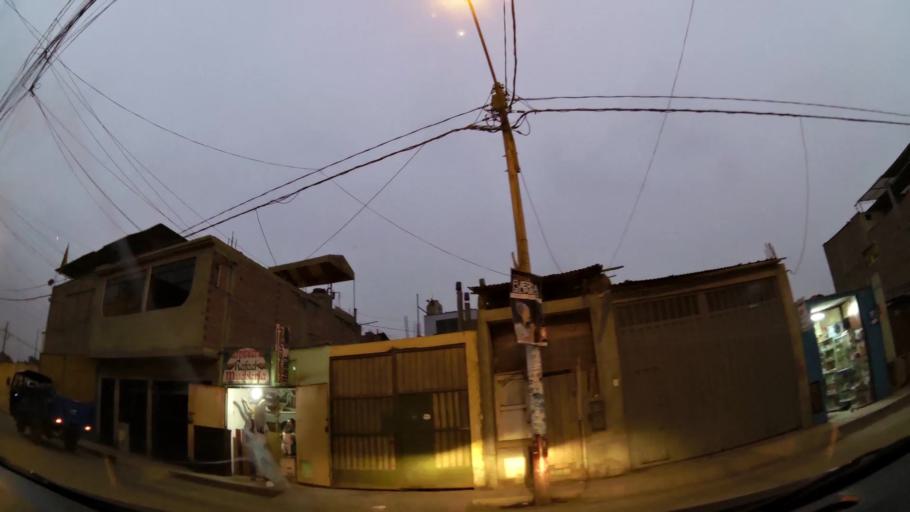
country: PE
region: Lima
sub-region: Lima
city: Surco
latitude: -12.1902
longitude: -76.9739
